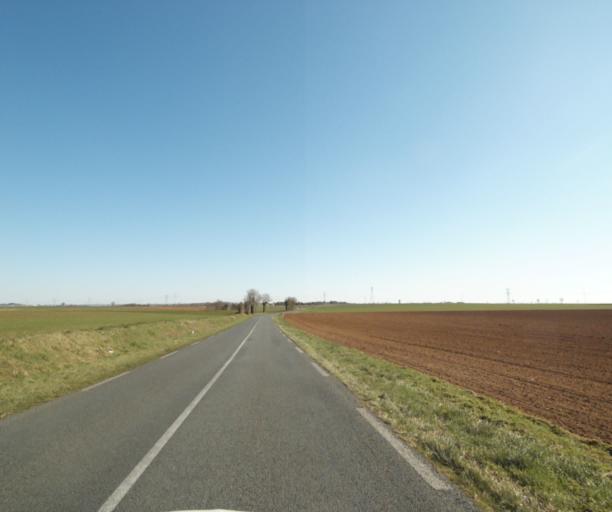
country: FR
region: Poitou-Charentes
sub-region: Departement des Deux-Sevres
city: Saint-Maxire
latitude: 46.3654
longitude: -0.4938
